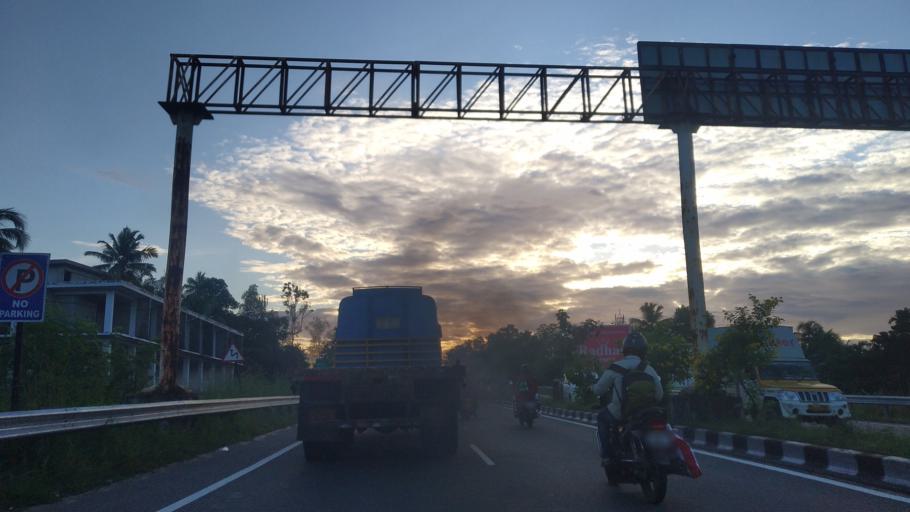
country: IN
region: Kerala
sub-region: Ernakulam
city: Elur
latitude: 10.0610
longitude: 76.2879
